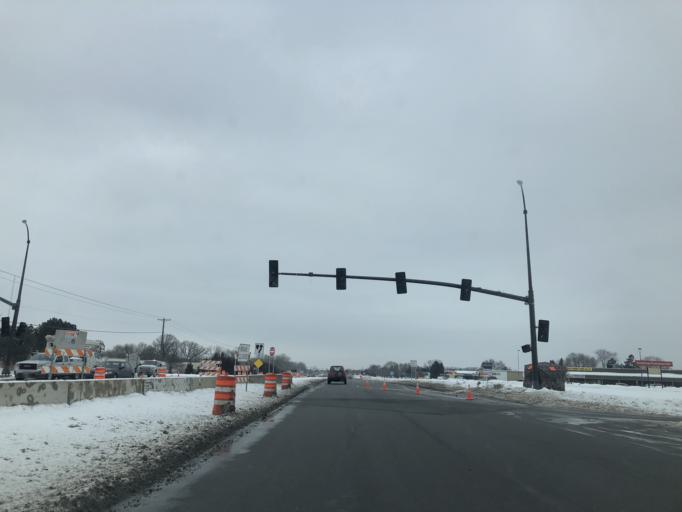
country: US
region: Minnesota
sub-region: Hennepin County
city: Brooklyn Park
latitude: 45.0872
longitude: -93.3795
